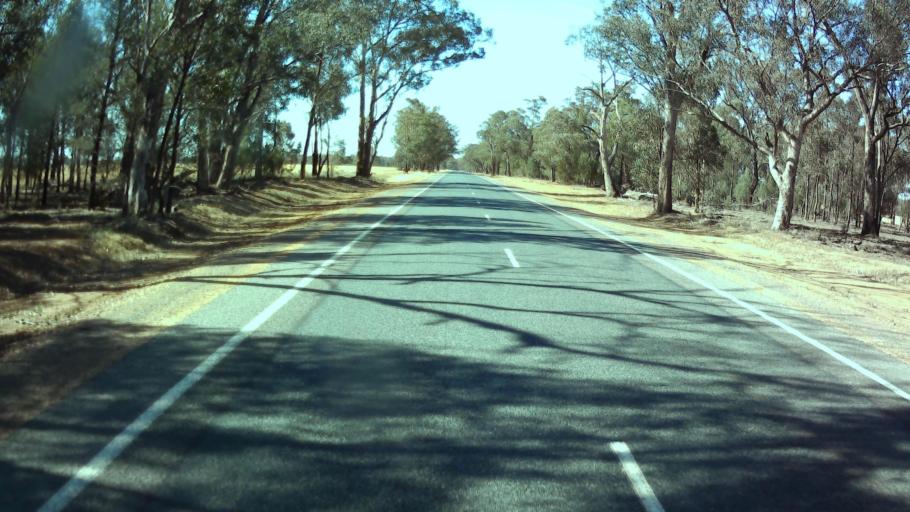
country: AU
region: New South Wales
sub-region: Weddin
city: Grenfell
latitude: -33.7409
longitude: 148.0887
